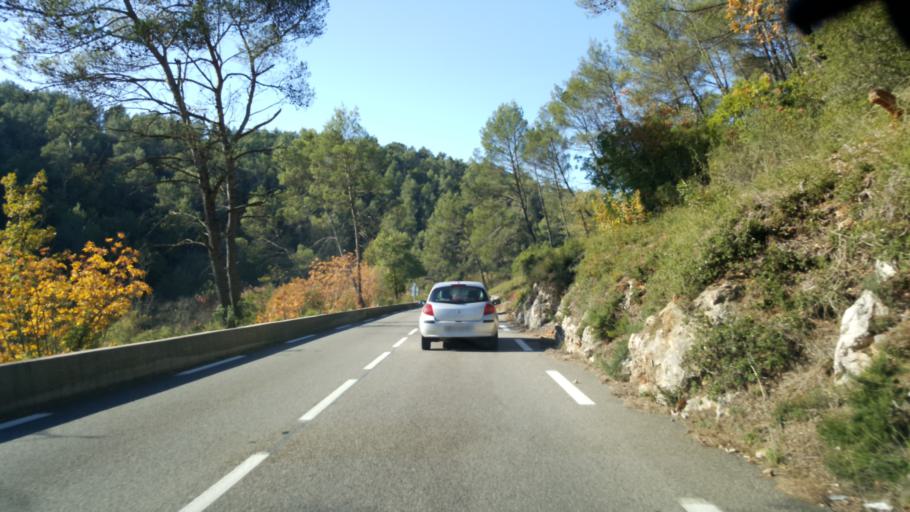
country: FR
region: Provence-Alpes-Cote d'Azur
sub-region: Departement du Var
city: Saint-Zacharie
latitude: 43.3823
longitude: 5.7385
